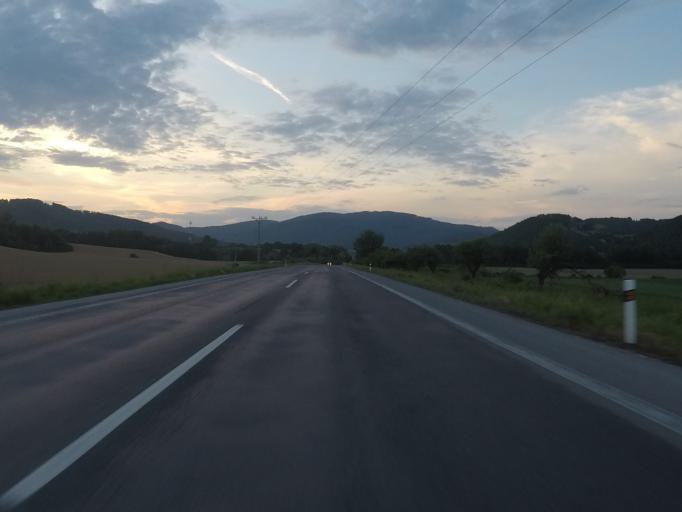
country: SK
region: Banskobystricky
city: Rimavska Sobota
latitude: 48.4876
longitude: 19.9433
